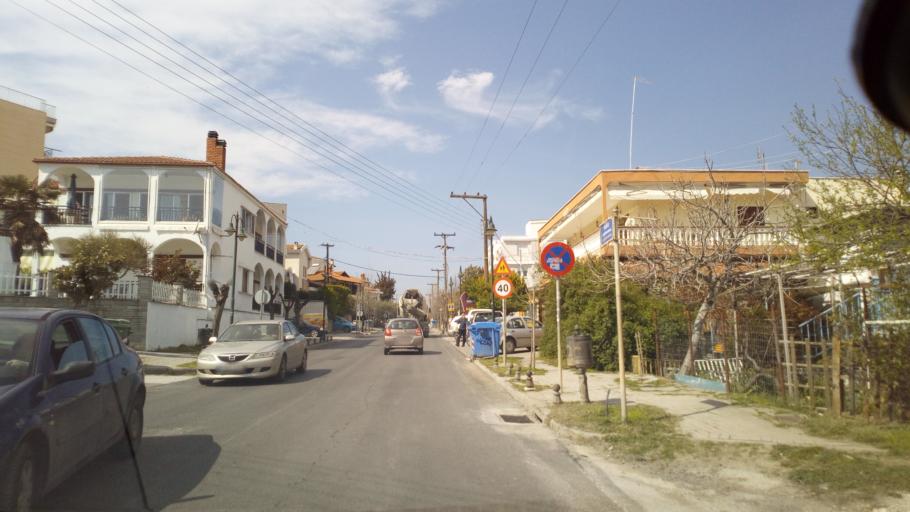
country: GR
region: Central Macedonia
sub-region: Nomos Thessalonikis
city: Thermi
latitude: 40.5472
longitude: 23.0262
